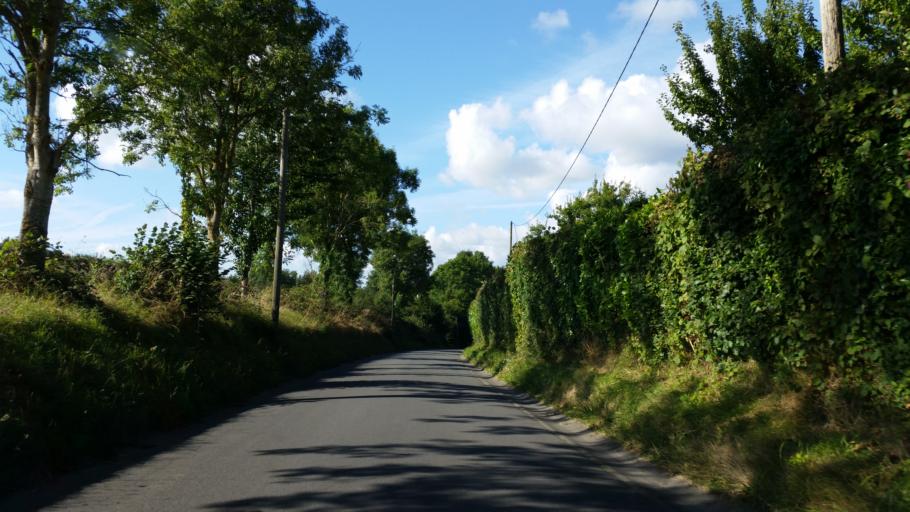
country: FR
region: Lower Normandy
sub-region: Departement du Calvados
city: Equemauville
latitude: 49.3865
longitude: 0.2264
